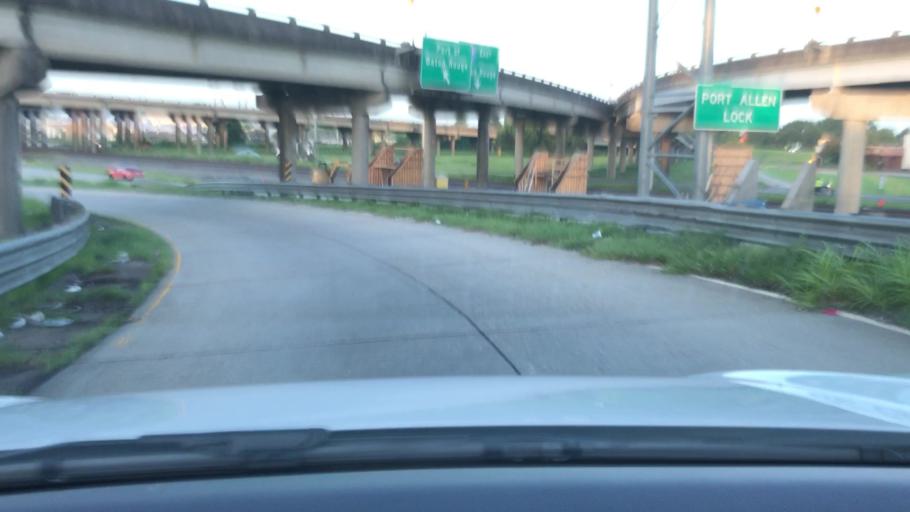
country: US
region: Louisiana
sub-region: West Baton Rouge Parish
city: Port Allen
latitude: 30.4417
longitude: -91.2097
